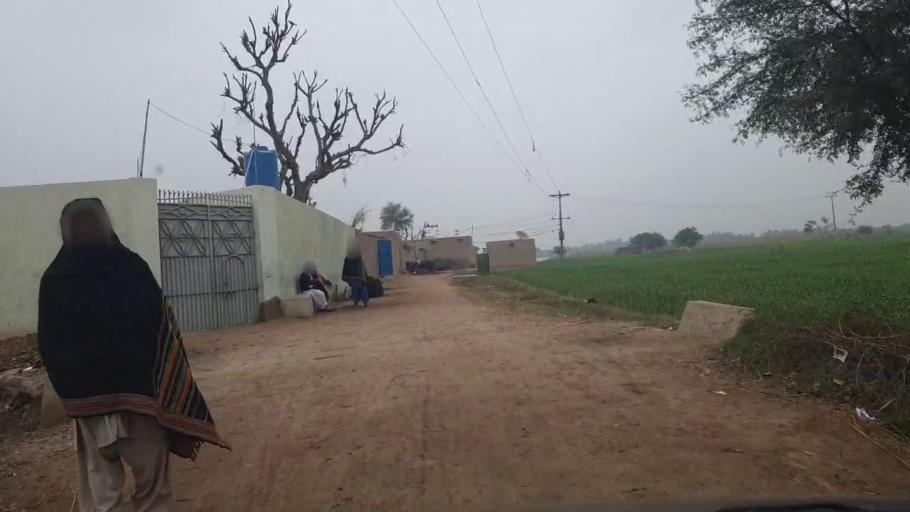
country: PK
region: Sindh
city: Tando Adam
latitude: 25.8514
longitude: 68.6760
